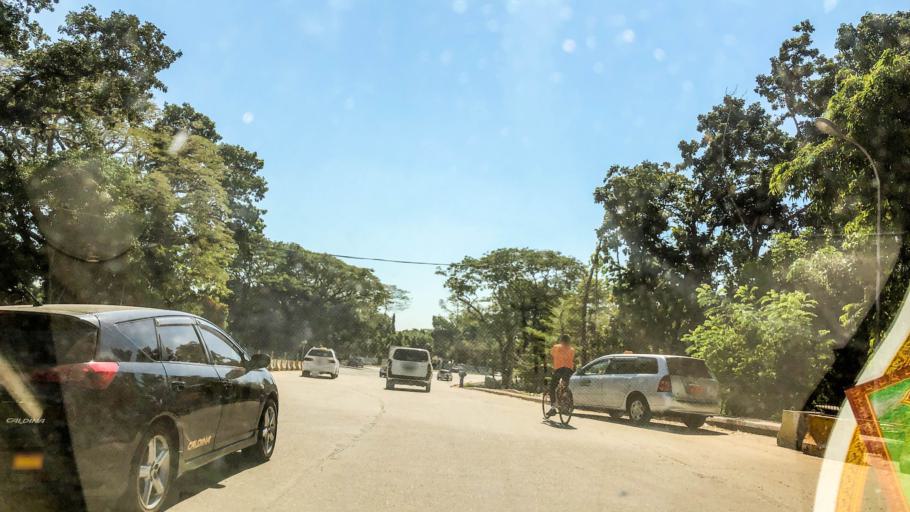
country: MM
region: Yangon
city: Yangon
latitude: 16.8971
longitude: 96.1316
